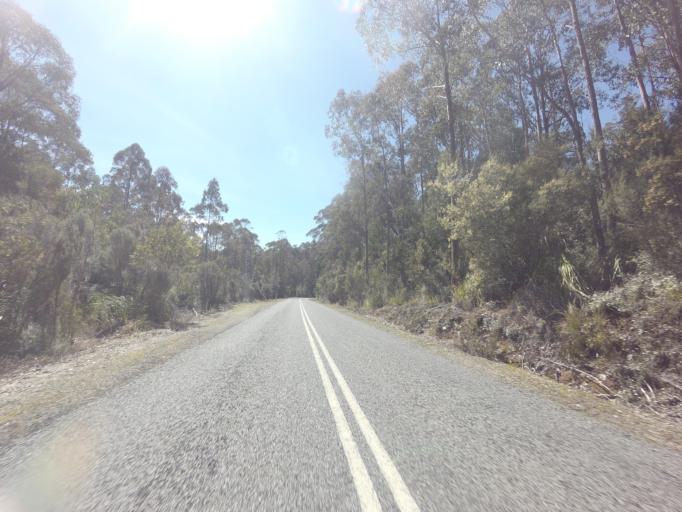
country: AU
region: Tasmania
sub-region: Huon Valley
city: Geeveston
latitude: -42.7811
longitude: 146.3990
